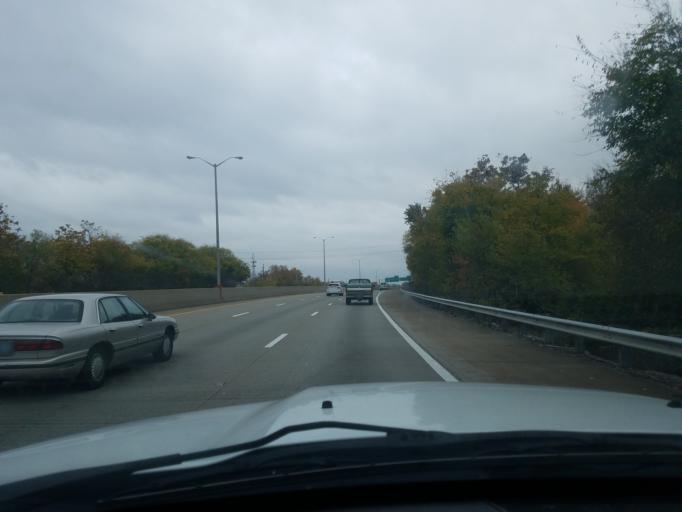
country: US
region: Indiana
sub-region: Floyd County
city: New Albany
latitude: 38.2620
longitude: -85.8052
